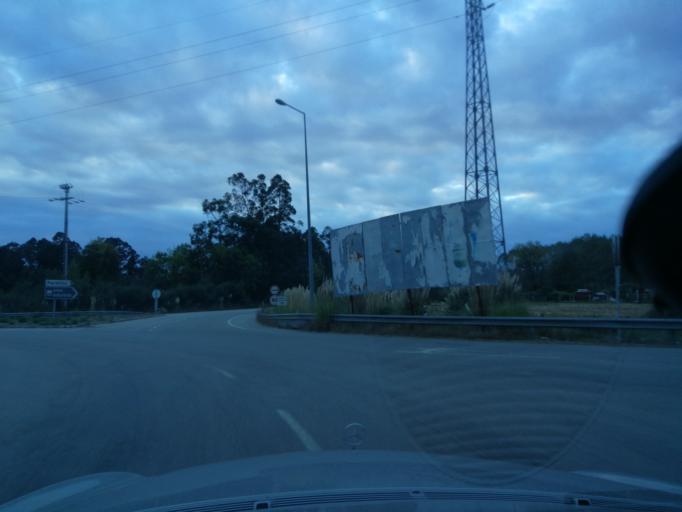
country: PT
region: Aveiro
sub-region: Estarreja
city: Beduido
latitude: 40.7827
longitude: -8.5655
